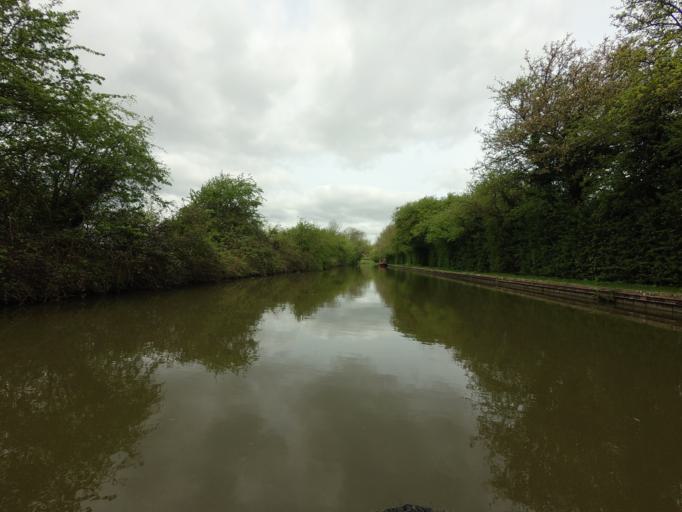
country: GB
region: England
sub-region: Milton Keynes
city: Simpson
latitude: 52.0144
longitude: -0.7191
